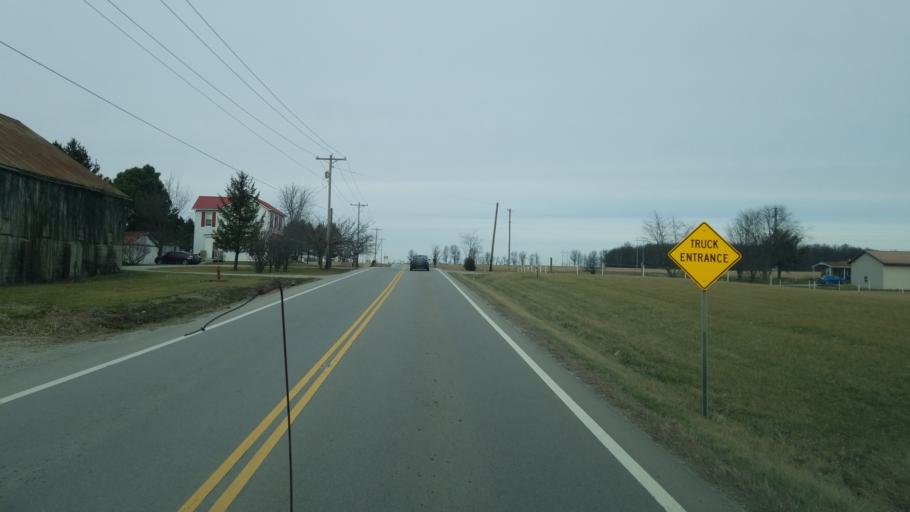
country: US
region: Ohio
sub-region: Adams County
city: Winchester
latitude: 39.0108
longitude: -83.7069
